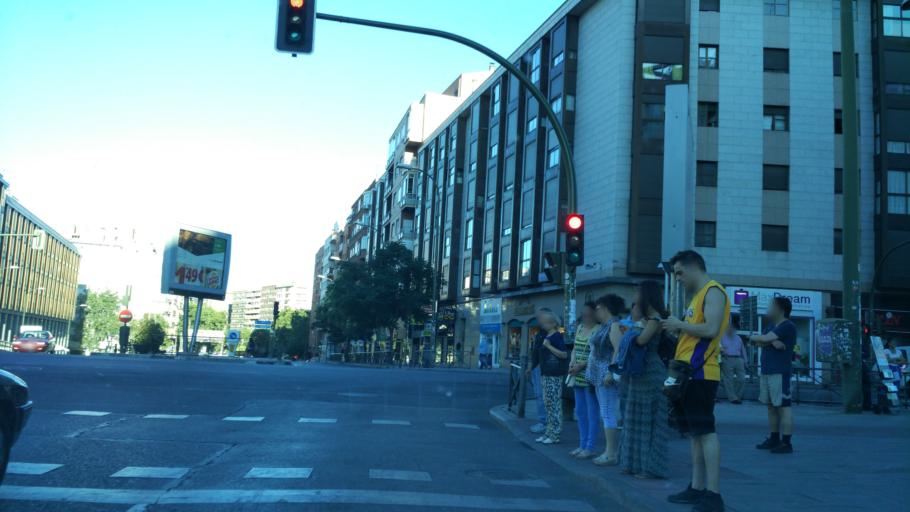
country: ES
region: Madrid
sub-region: Provincia de Madrid
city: Tetuan de las Victorias
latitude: 40.4607
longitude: -3.6987
